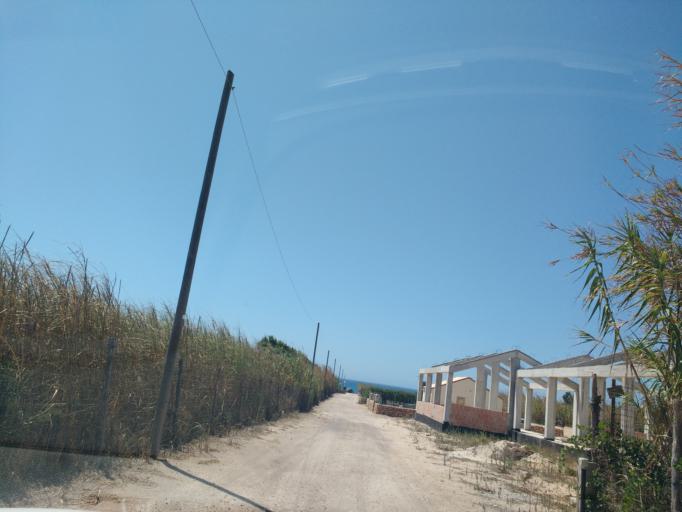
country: IT
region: Sicily
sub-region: Provincia di Siracusa
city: Portopalo di Capo Passero
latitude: 36.6526
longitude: 15.0816
